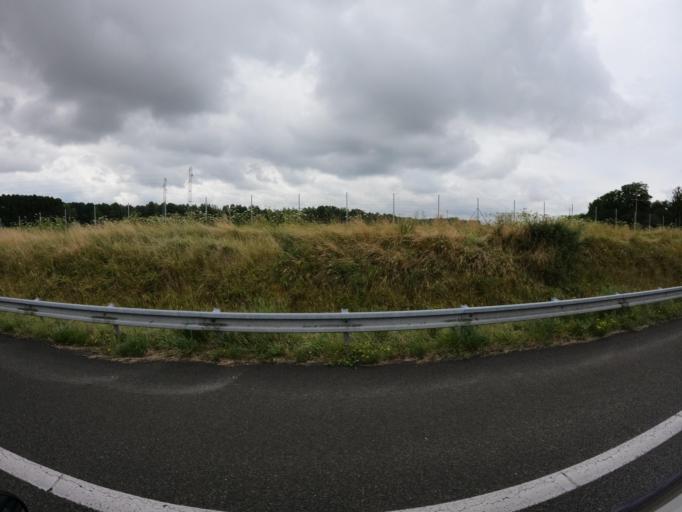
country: FR
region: Centre
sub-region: Departement du Loir-et-Cher
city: Saint-Sulpice-de-Pommeray
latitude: 47.6190
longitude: 1.2500
